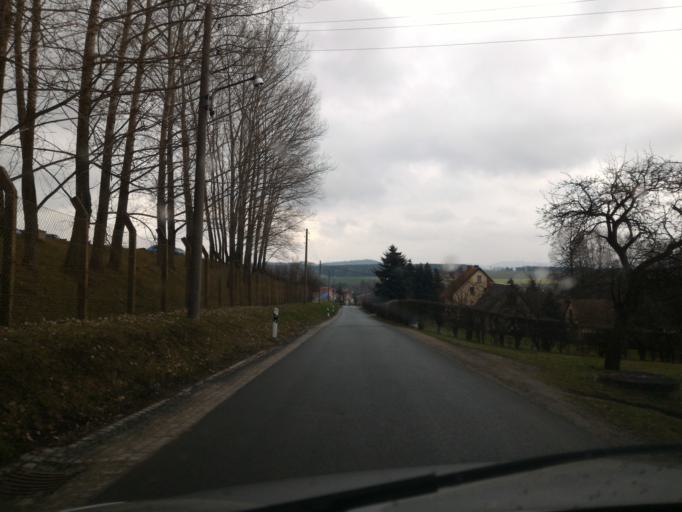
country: DE
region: Saxony
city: Hainewalde
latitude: 50.9441
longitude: 14.6845
